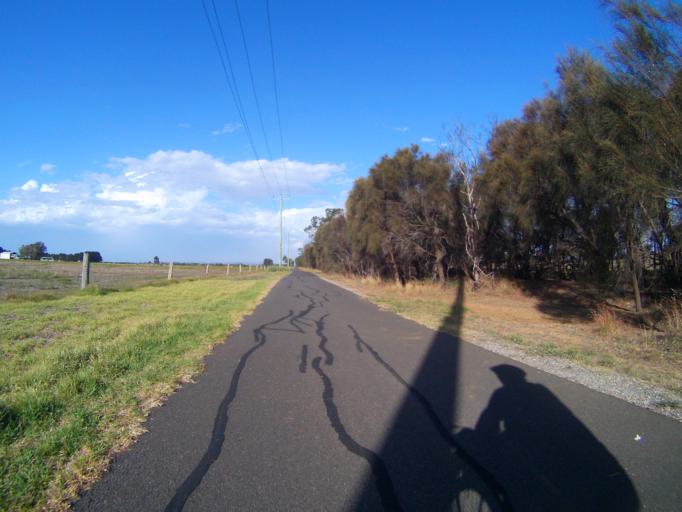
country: AU
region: Victoria
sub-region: Greater Geelong
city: Leopold
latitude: -38.1830
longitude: 144.4849
